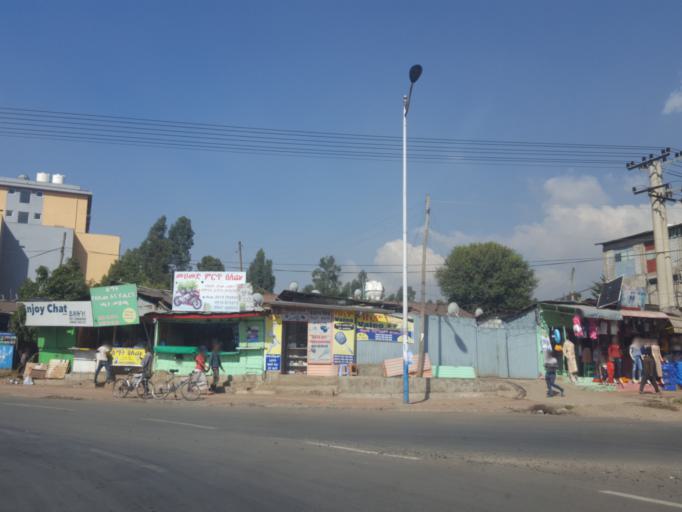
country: ET
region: Adis Abeba
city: Addis Ababa
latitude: 9.0491
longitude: 38.7379
